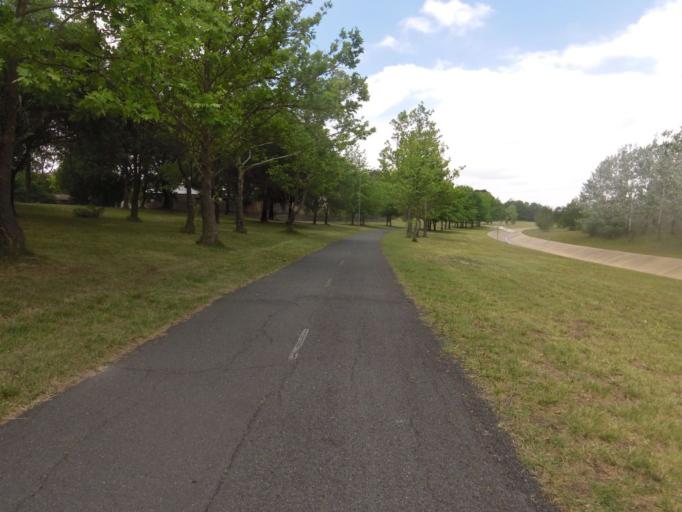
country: AU
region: Australian Capital Territory
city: Macarthur
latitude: -35.4195
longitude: 149.1059
